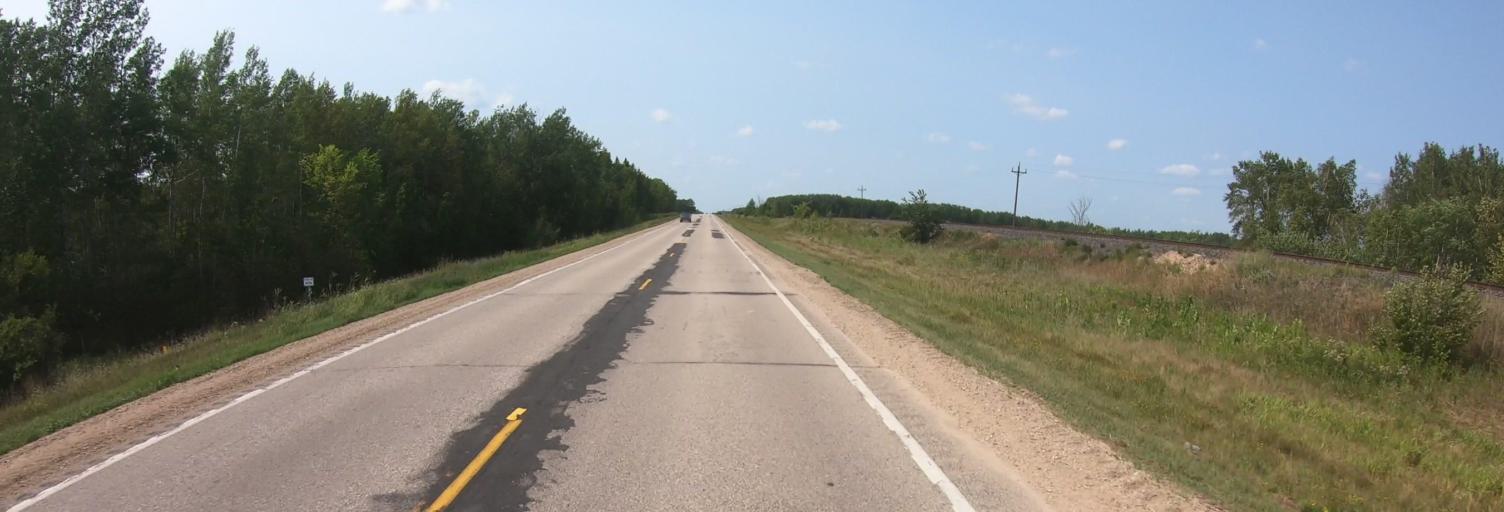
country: US
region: Minnesota
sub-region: Lake of the Woods County
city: Baudette
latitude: 48.7451
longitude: -94.8585
